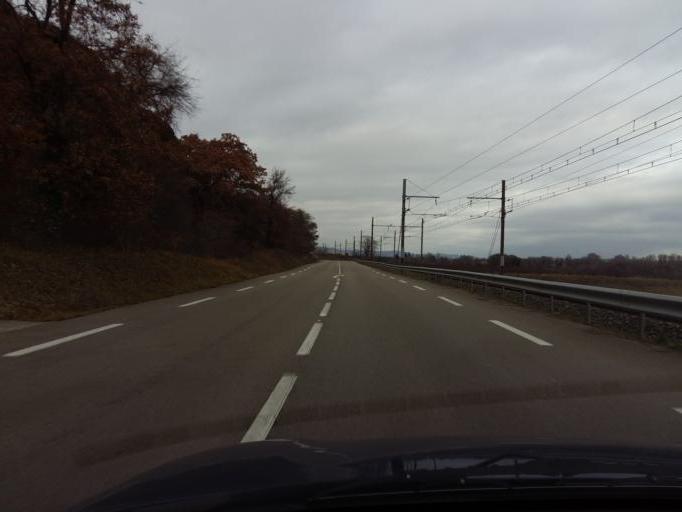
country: FR
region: Rhone-Alpes
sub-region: Departement de l'Ardeche
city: Cornas
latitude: 44.9887
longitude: 4.8474
